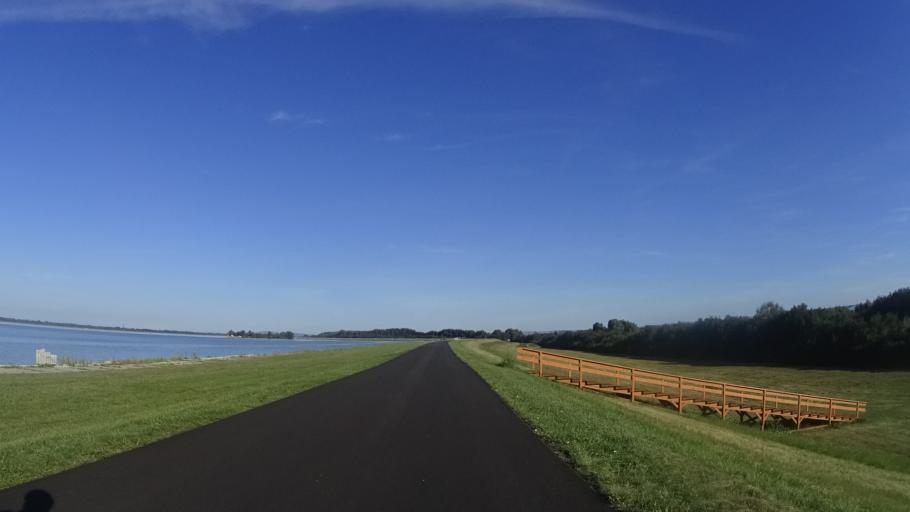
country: SK
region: Trnavsky
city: Samorin
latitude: 48.0148
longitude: 17.2960
